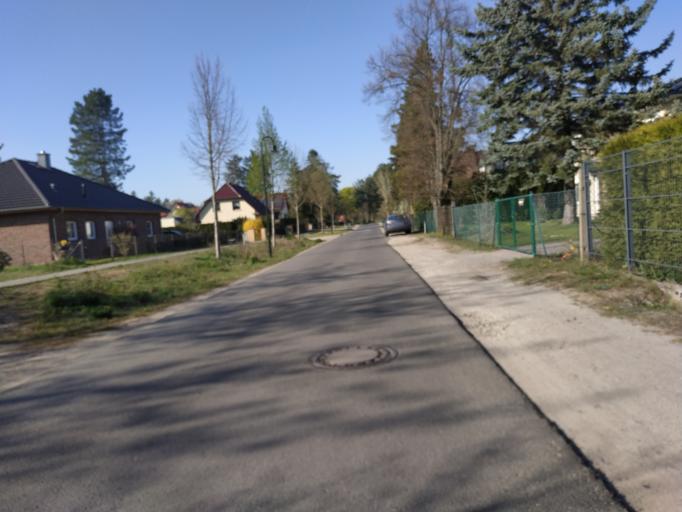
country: DE
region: Brandenburg
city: Petershagen
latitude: 52.5441
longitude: 13.8233
